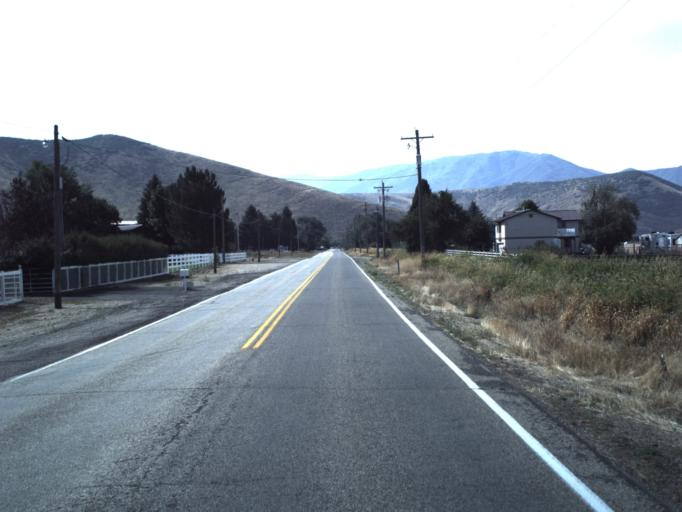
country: US
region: Utah
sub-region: Wasatch County
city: Midway
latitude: 40.4678
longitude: -111.4718
